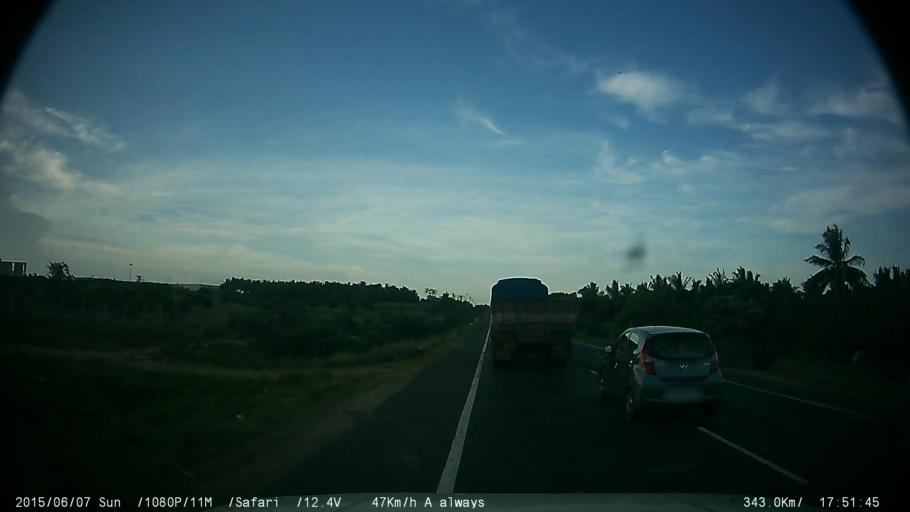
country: IN
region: Tamil Nadu
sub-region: Coimbatore
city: Madukkarai
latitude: 10.9270
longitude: 76.9953
